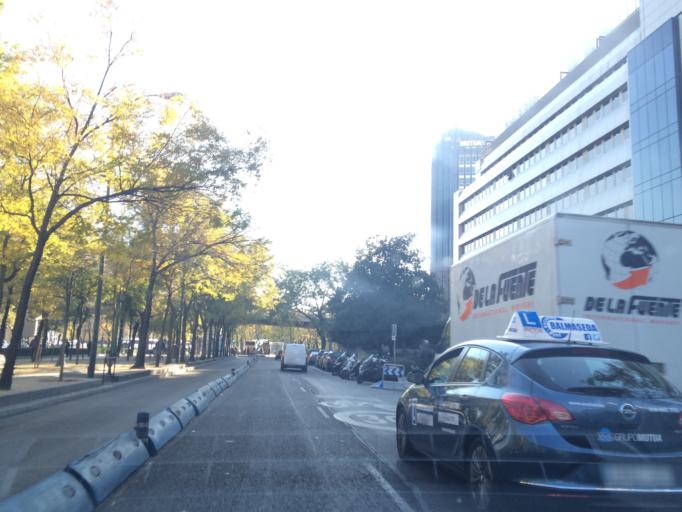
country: ES
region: Madrid
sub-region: Provincia de Madrid
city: Salamanca
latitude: 40.4343
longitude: -3.6890
